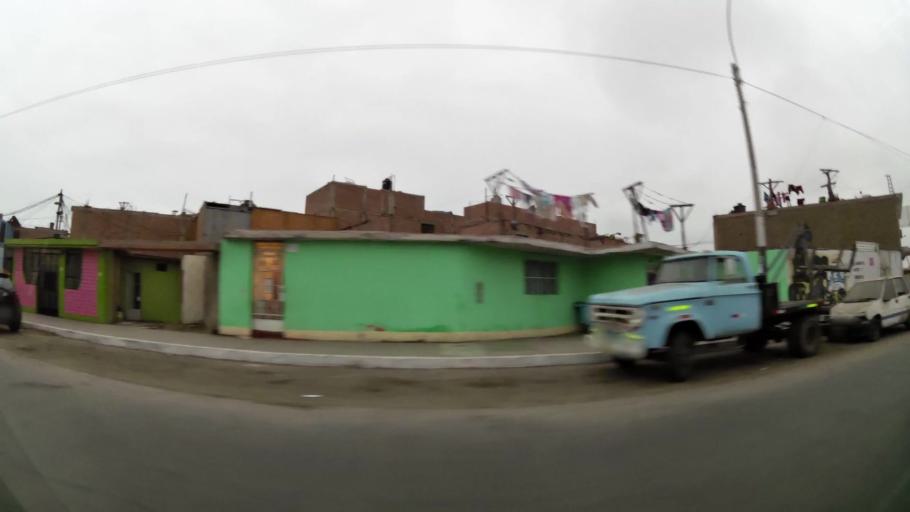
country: PE
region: Callao
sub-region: Callao
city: Callao
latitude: -12.0605
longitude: -77.1084
